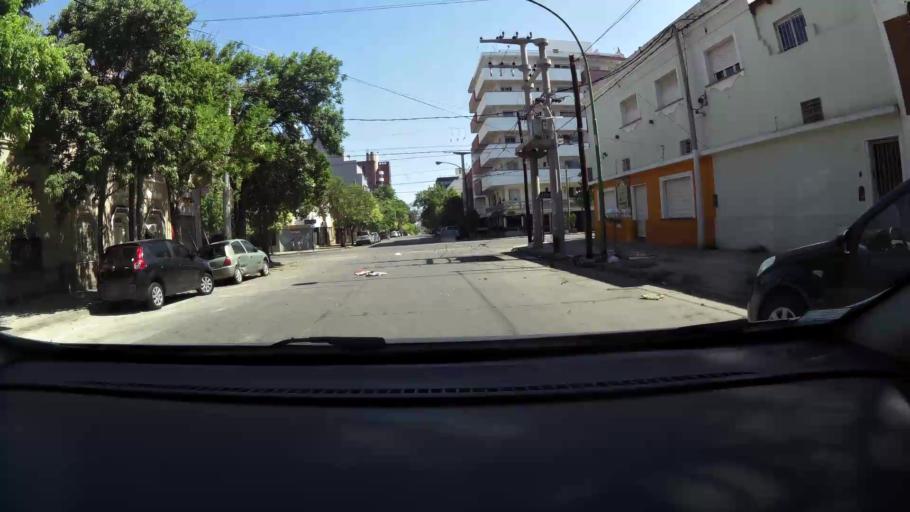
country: AR
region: Cordoba
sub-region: Departamento de Capital
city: Cordoba
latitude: -31.4002
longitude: -64.1785
